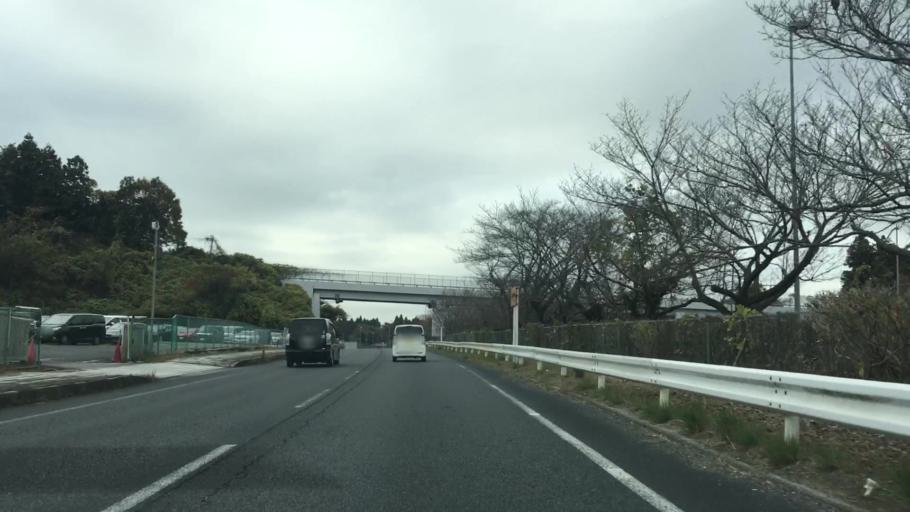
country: JP
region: Chiba
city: Narita
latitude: 35.7854
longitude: 140.3667
